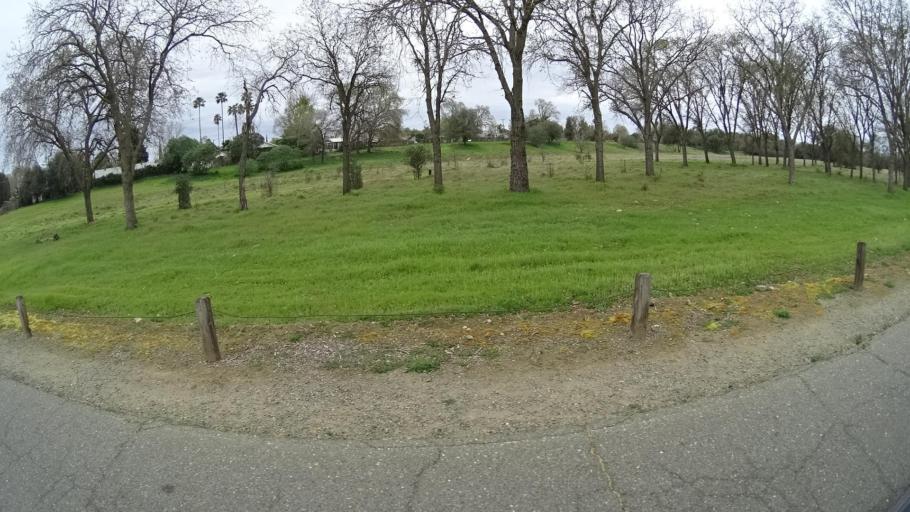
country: US
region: California
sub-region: Sacramento County
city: Fair Oaks
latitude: 38.6190
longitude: -121.2872
